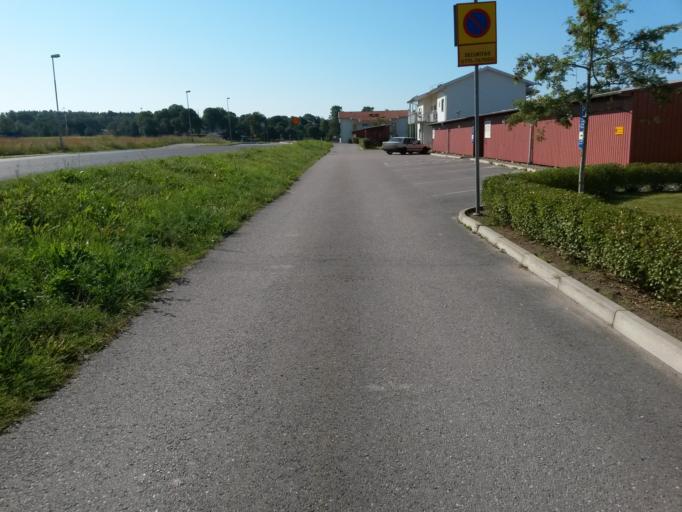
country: SE
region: Vaestra Goetaland
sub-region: Vargarda Kommun
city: Vargarda
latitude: 58.0215
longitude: 12.8139
